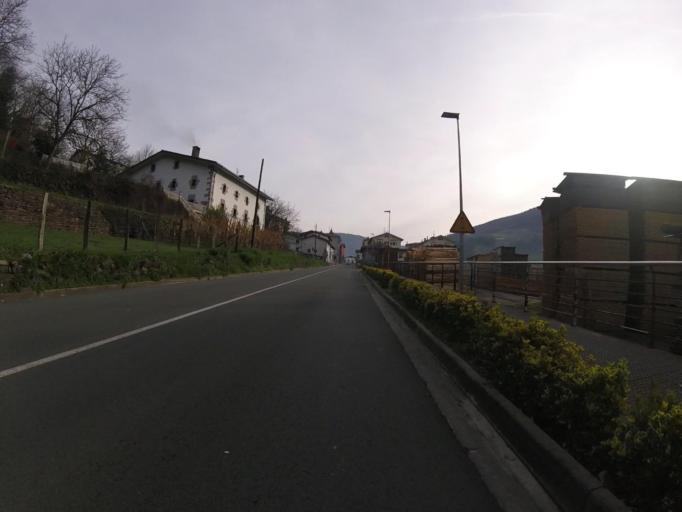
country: ES
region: Basque Country
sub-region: Provincia de Guipuzcoa
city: Berrobi
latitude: 43.1459
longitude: -2.0290
